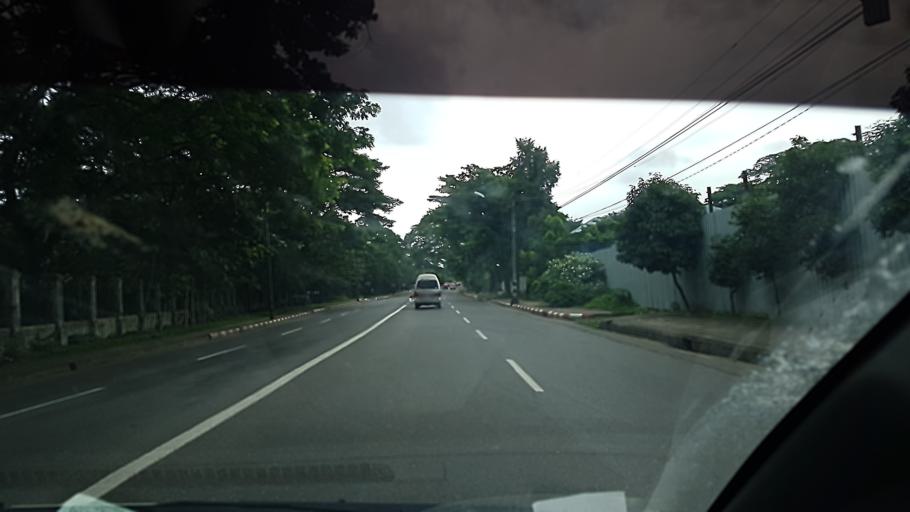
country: MM
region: Yangon
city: Yangon
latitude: 16.7919
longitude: 96.1369
